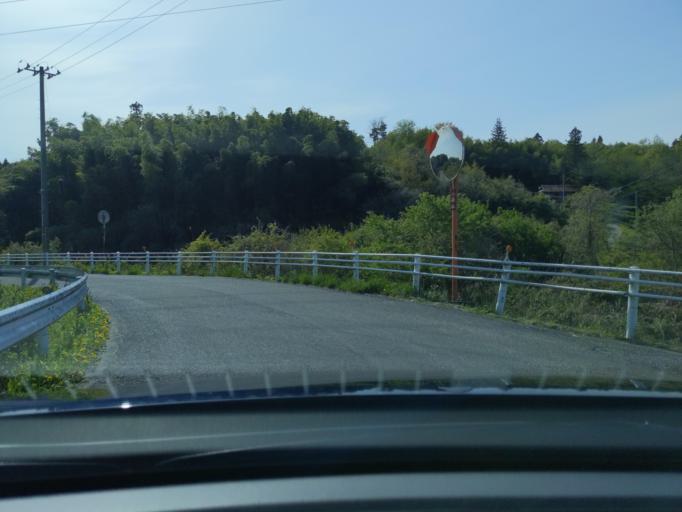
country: JP
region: Fukushima
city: Sukagawa
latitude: 37.2974
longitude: 140.4172
